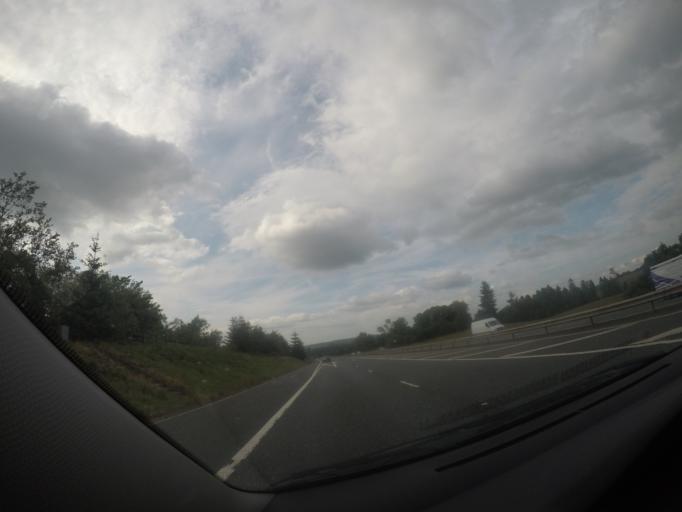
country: GB
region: Scotland
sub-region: South Lanarkshire
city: Douglas
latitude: 55.5693
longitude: -3.8086
